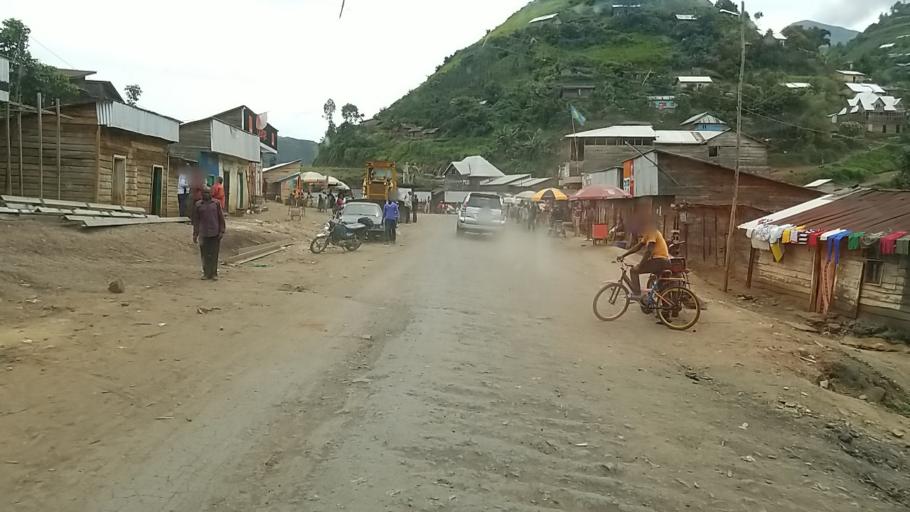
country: CD
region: Nord Kivu
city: Sake
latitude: -1.7562
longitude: 28.9848
